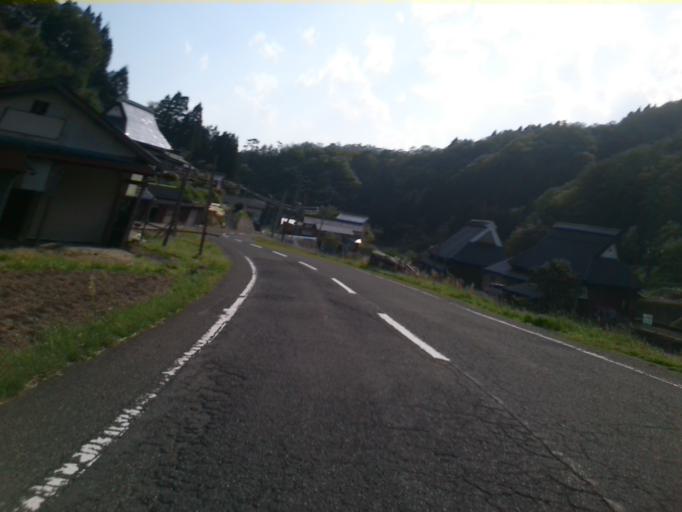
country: JP
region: Kyoto
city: Miyazu
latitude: 35.6963
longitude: 135.1727
